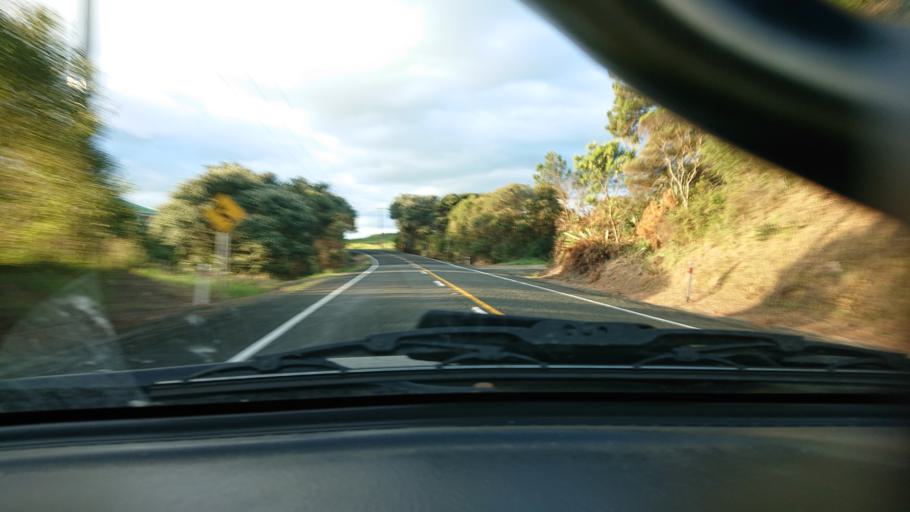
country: NZ
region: Auckland
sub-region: Auckland
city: Parakai
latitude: -36.5014
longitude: 174.4538
